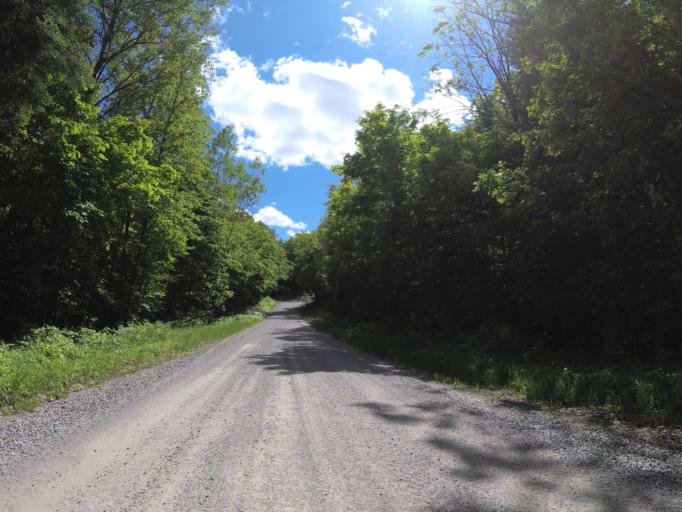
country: CA
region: Ontario
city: Renfrew
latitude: 45.0435
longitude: -76.8218
